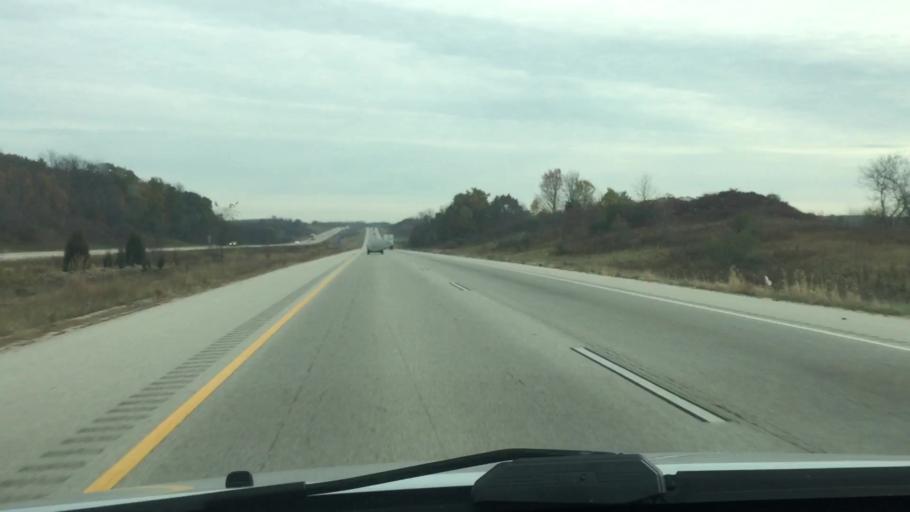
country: US
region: Wisconsin
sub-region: Waukesha County
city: Big Bend
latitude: 42.8879
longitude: -88.2707
